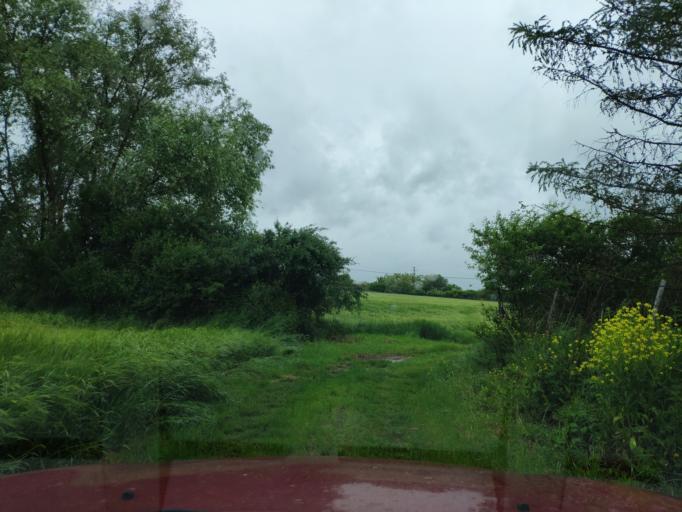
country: SK
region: Kosicky
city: Cierna nad Tisou
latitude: 48.4273
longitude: 22.0918
